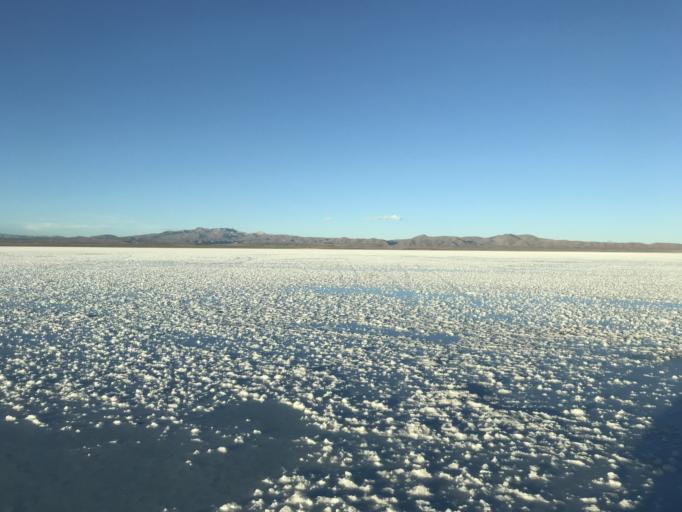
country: BO
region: Potosi
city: Colchani
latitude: -20.3842
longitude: -66.9855
